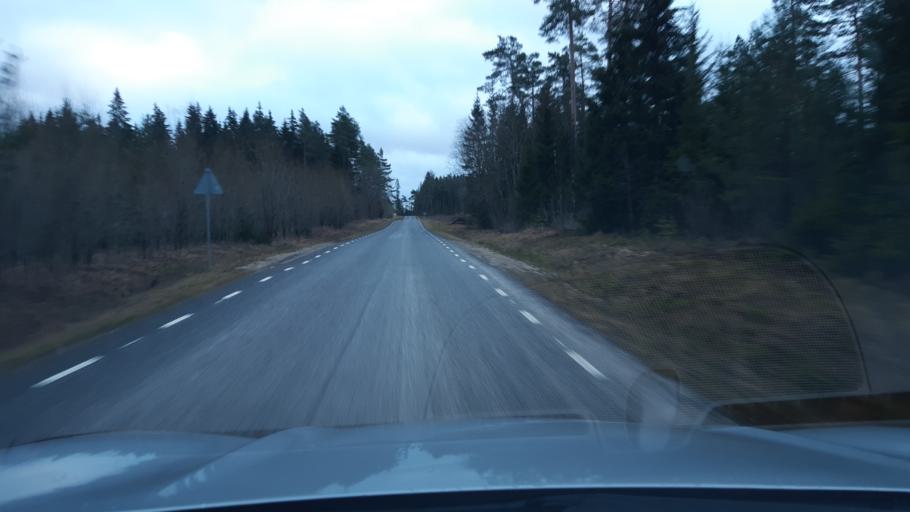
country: EE
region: Raplamaa
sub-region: Kohila vald
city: Kohila
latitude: 59.1688
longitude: 24.6251
